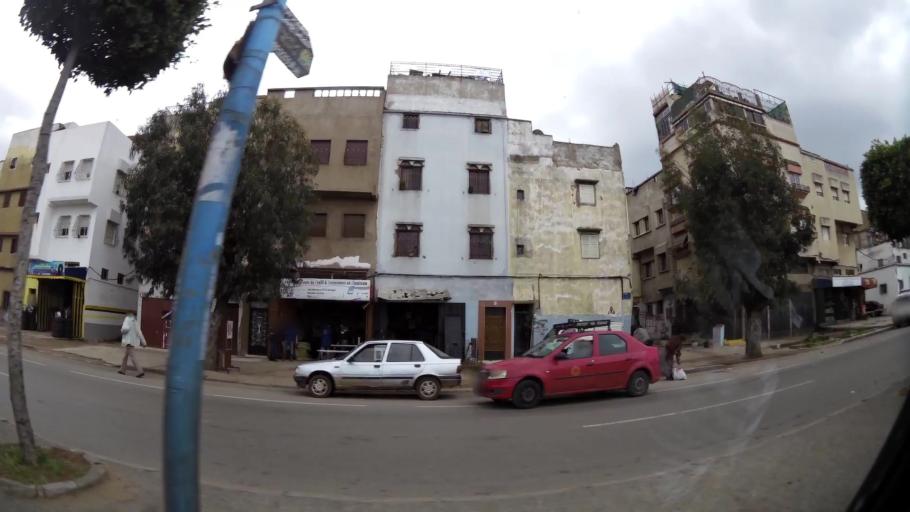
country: MA
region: Grand Casablanca
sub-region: Casablanca
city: Casablanca
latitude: 33.5594
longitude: -7.5546
